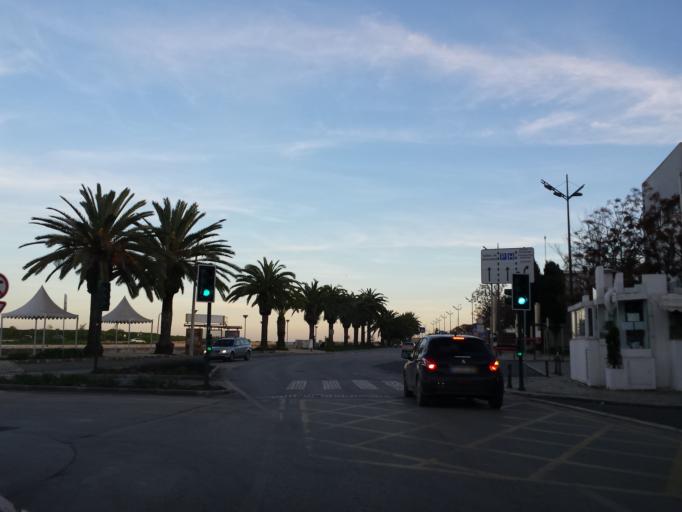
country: PT
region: Faro
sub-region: Lagos
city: Lagos
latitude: 37.1036
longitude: -8.6725
